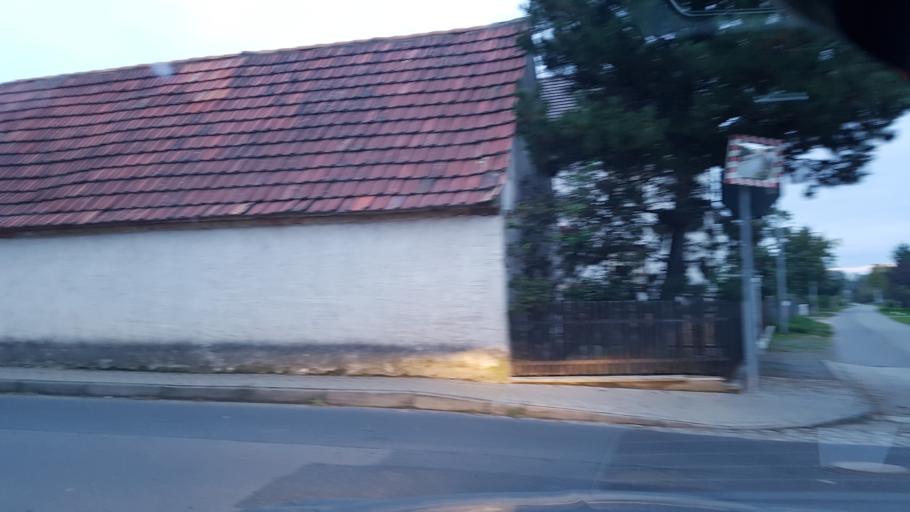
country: DE
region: Brandenburg
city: Hirschfeld
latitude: 51.3876
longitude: 13.6156
